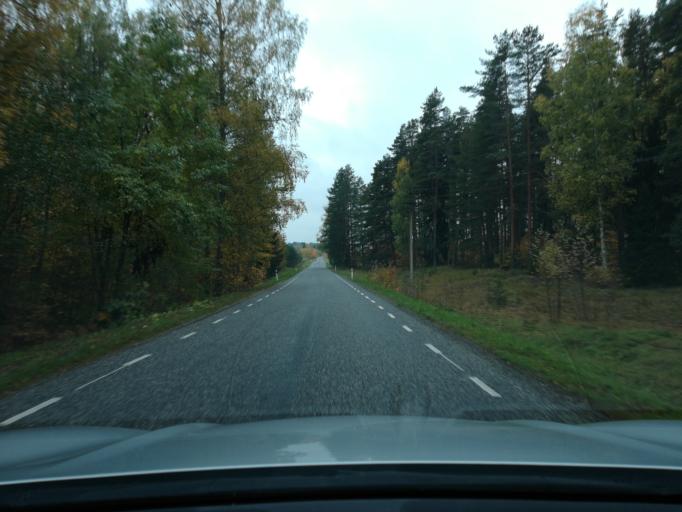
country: EE
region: Ida-Virumaa
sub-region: Johvi vald
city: Johvi
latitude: 59.1520
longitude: 27.3817
